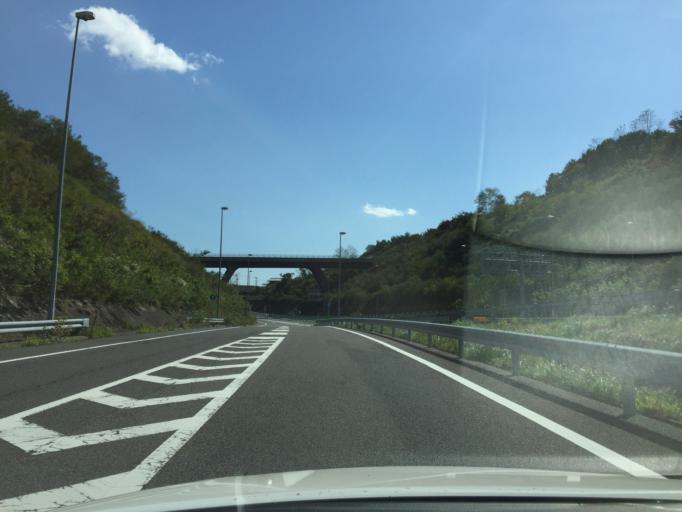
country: JP
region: Fukushima
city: Sukagawa
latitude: 37.1903
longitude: 140.3003
